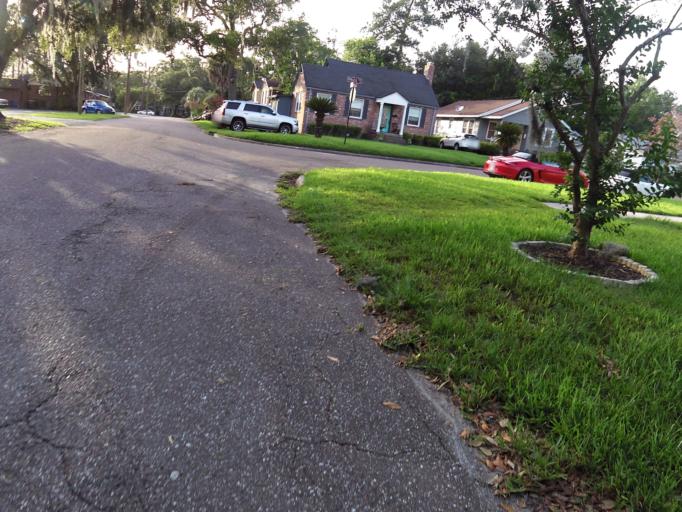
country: US
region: Florida
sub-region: Duval County
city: Jacksonville
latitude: 30.2982
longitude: -81.7107
